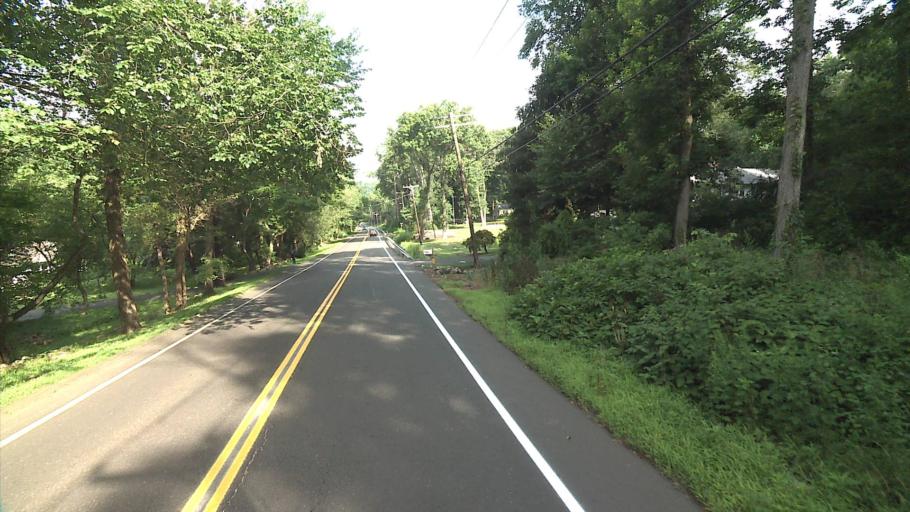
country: US
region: Connecticut
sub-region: New Haven County
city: Woodbridge
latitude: 41.3443
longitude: -73.0170
